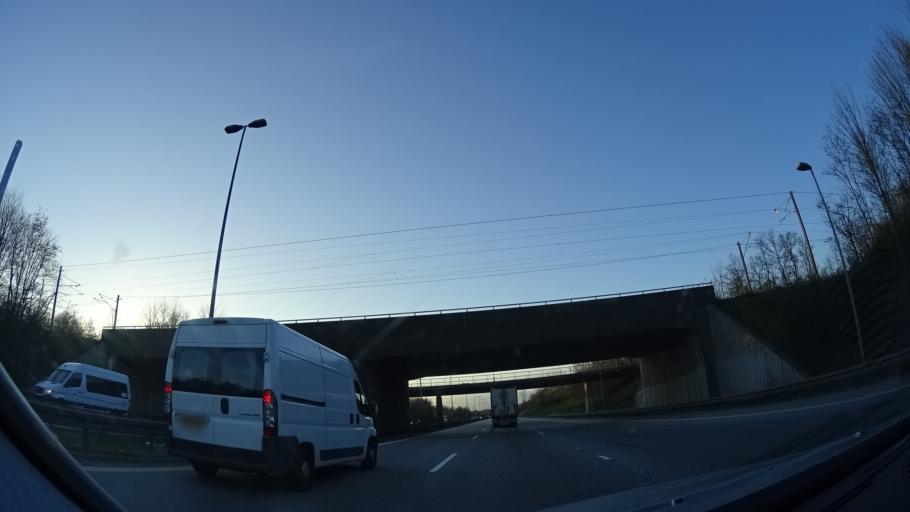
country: DK
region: Capital Region
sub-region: Brondby Kommune
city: Brondbyvester
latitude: 55.6217
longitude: 12.4419
